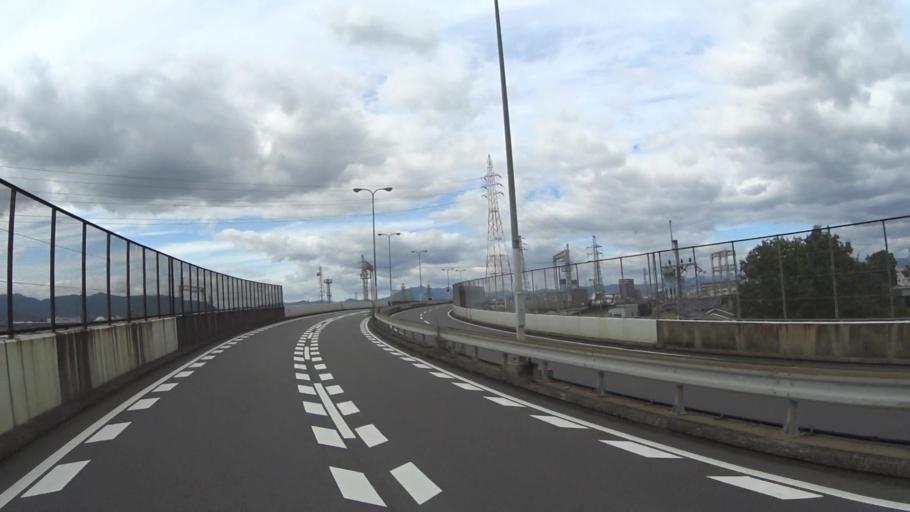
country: JP
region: Kyoto
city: Uji
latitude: 34.9245
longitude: 135.7554
